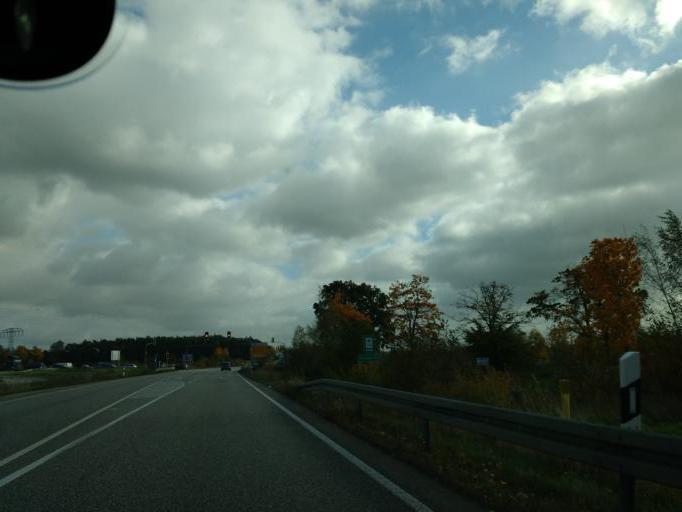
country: DE
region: Brandenburg
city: Neuenhagen
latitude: 52.5520
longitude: 13.6935
